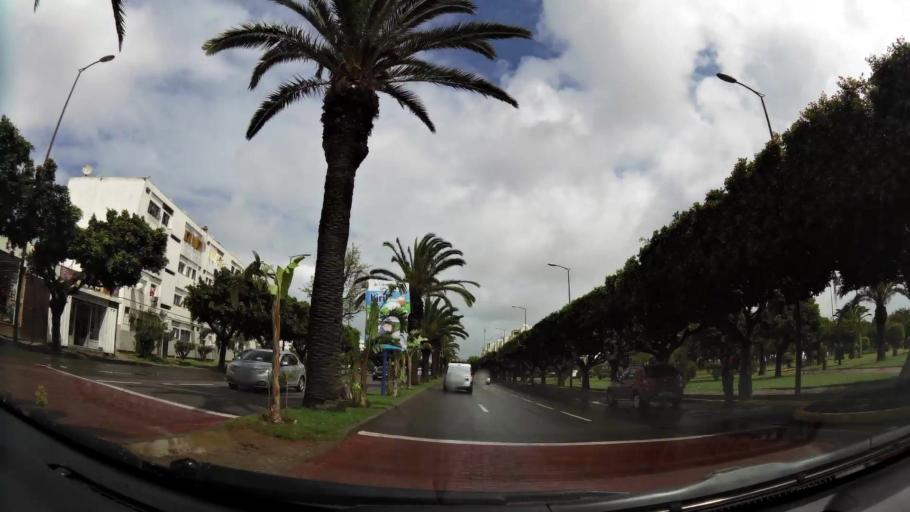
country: MA
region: Grand Casablanca
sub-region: Casablanca
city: Casablanca
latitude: 33.5682
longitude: -7.6366
